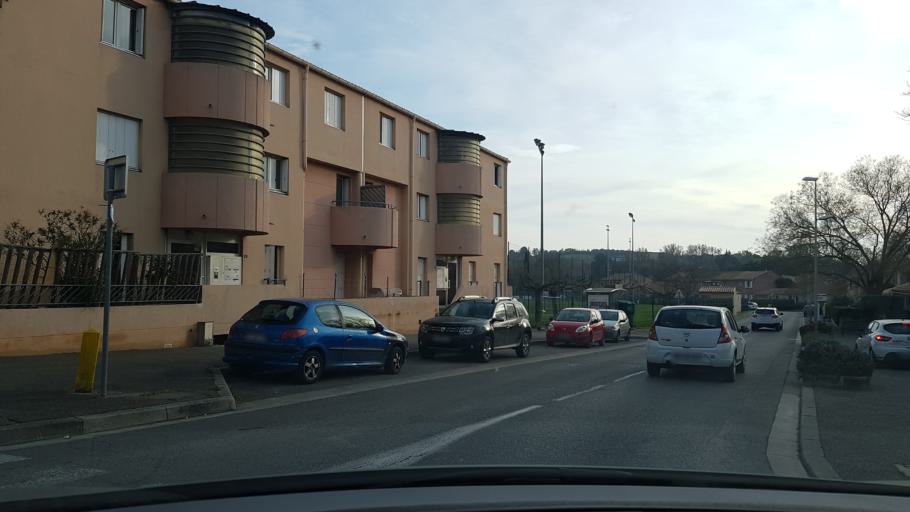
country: FR
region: Provence-Alpes-Cote d'Azur
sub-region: Departement des Bouches-du-Rhone
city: Bouc-Bel-Air
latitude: 43.4866
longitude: 5.4159
